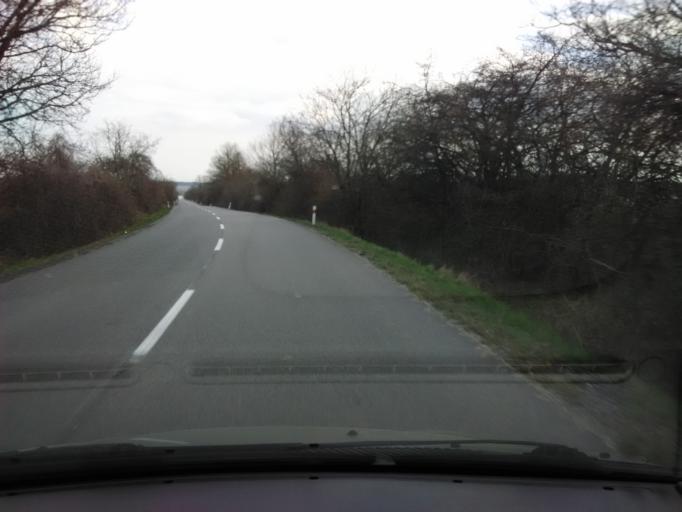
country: SK
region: Nitriansky
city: Tlmace
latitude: 48.3408
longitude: 18.4863
